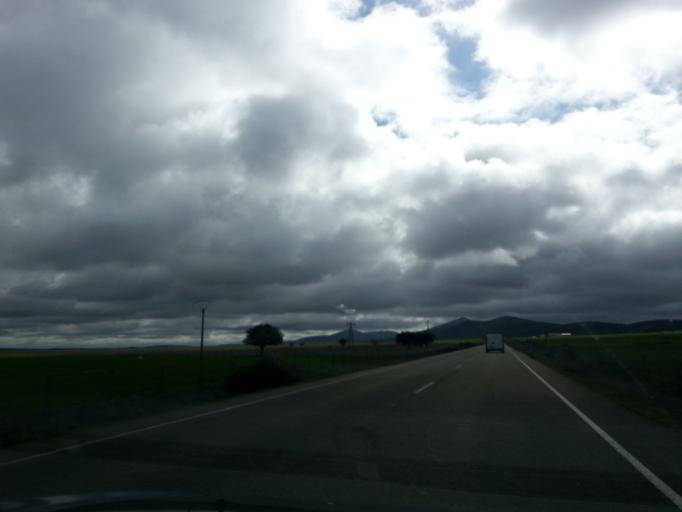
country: ES
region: Castille and Leon
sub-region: Provincia de Salamanca
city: Tamames
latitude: 40.6741
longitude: -6.1230
